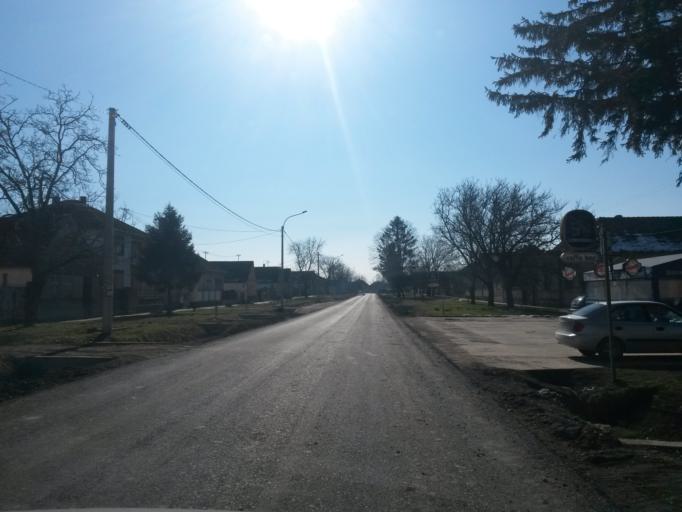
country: HR
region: Vukovarsko-Srijemska
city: Negoslavci
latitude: 45.2754
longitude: 18.9977
